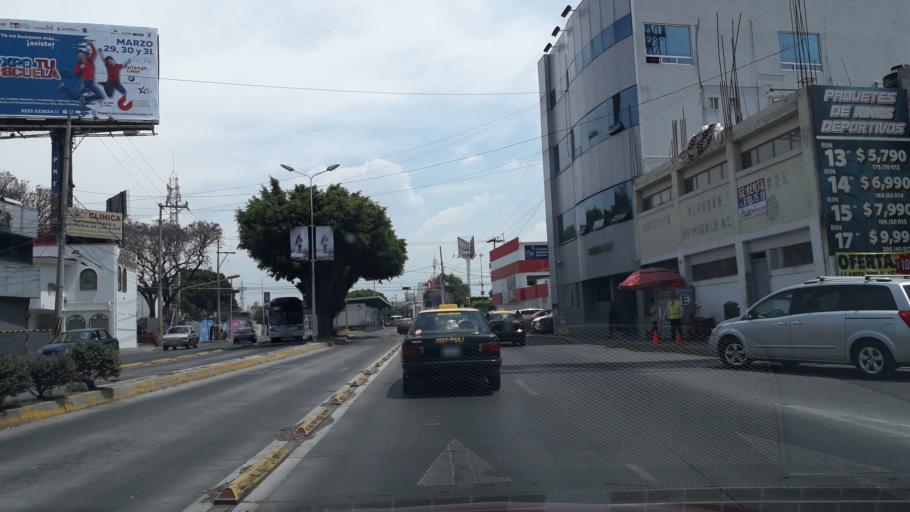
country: MX
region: Puebla
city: Puebla
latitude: 19.0352
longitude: -98.2141
